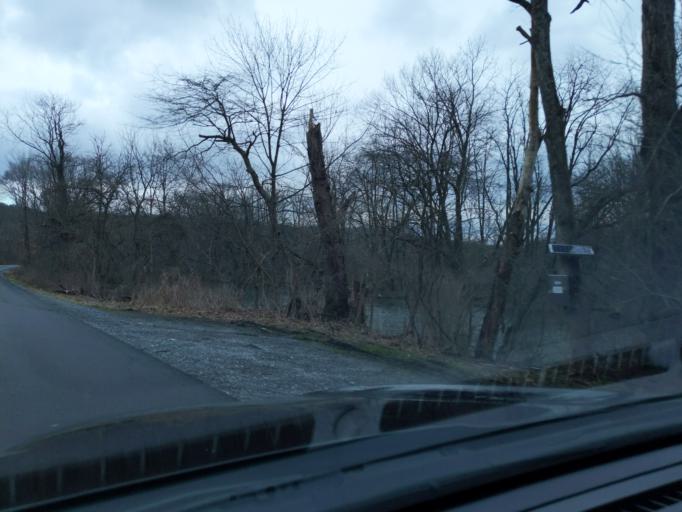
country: US
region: Pennsylvania
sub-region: Blair County
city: Bellwood
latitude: 40.6225
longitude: -78.3188
